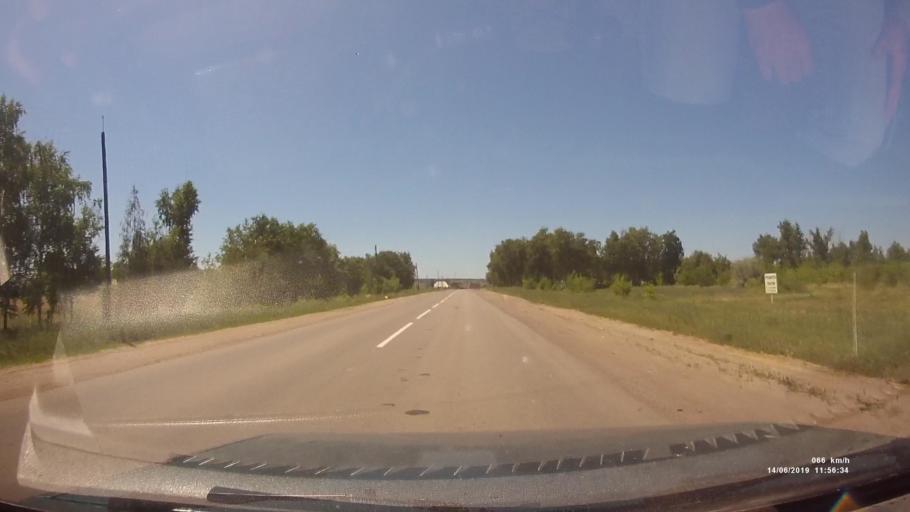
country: RU
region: Rostov
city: Kazanskaya
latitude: 49.8022
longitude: 41.1599
